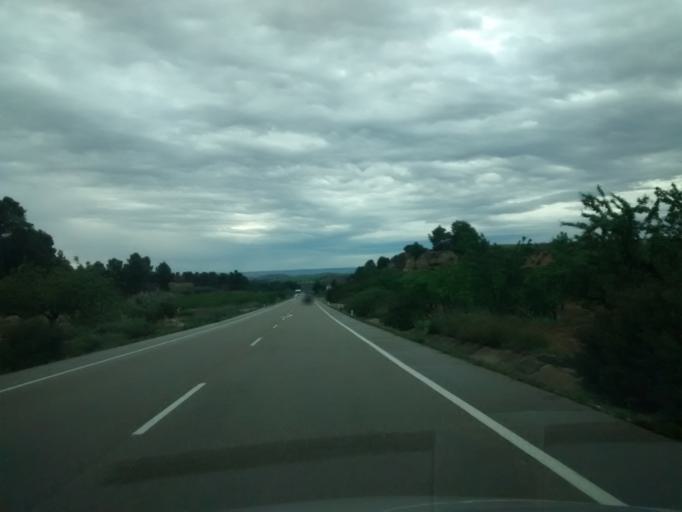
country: ES
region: Aragon
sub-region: Provincia de Zaragoza
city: Maella
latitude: 41.1630
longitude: 0.0797
